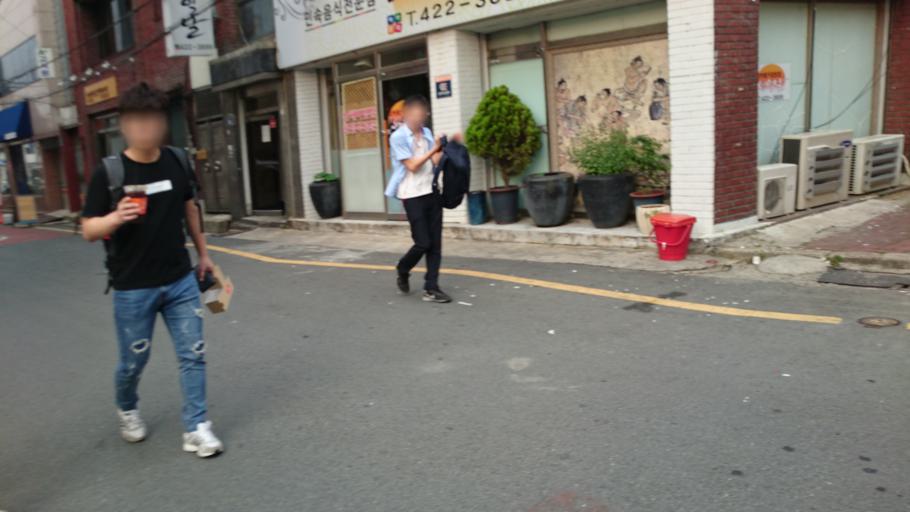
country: KR
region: Daegu
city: Daegu
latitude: 35.8631
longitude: 128.5986
